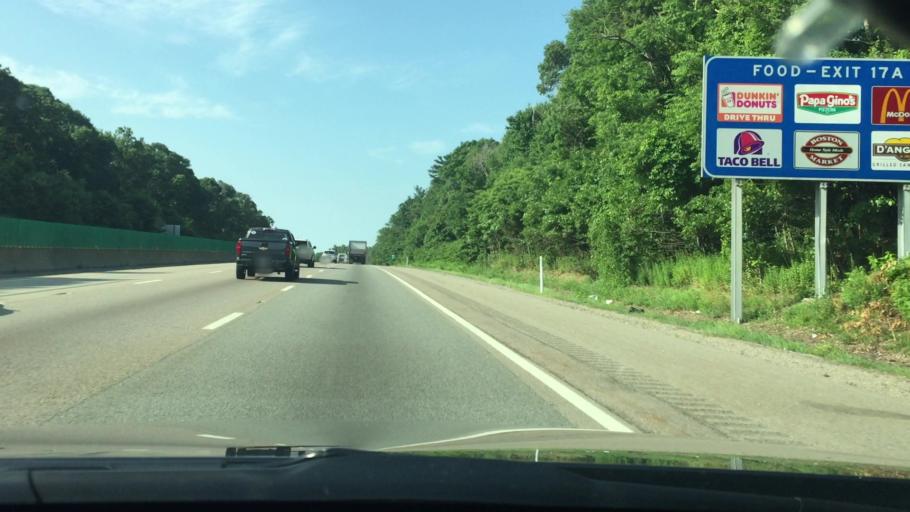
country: US
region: Massachusetts
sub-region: Plymouth County
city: Brockton
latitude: 42.0860
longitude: -71.0616
